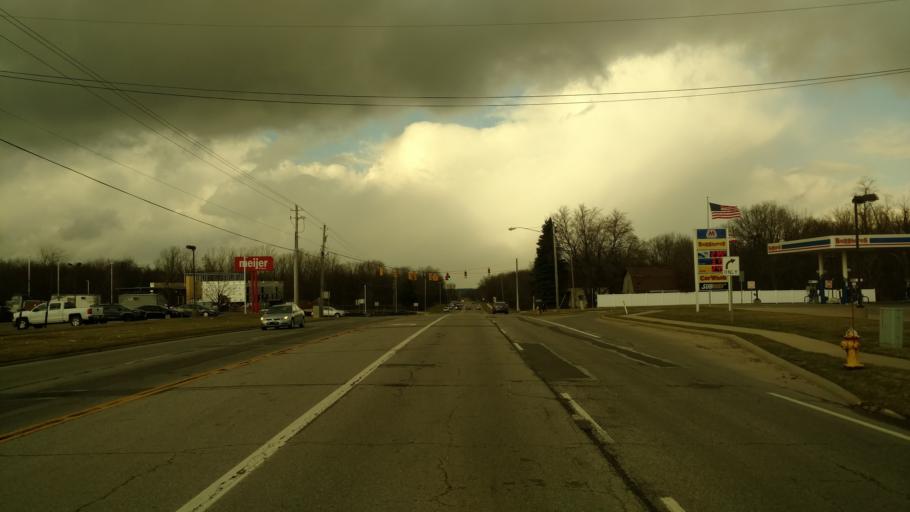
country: US
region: Ohio
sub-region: Richland County
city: Ontario
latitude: 40.7886
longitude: -82.5901
